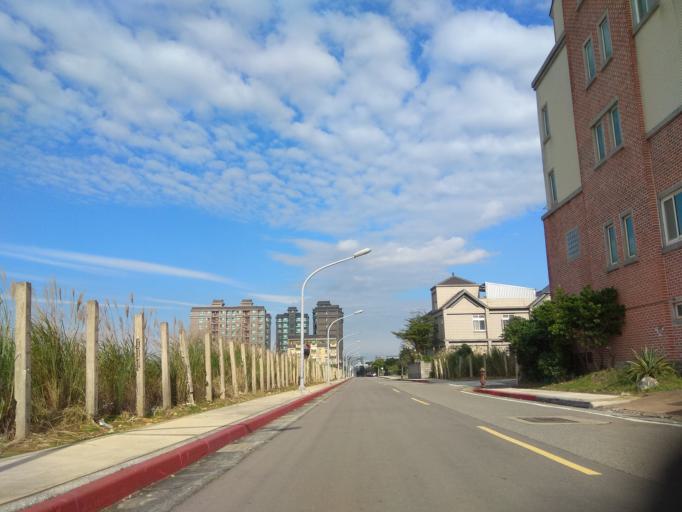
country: TW
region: Taiwan
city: Taoyuan City
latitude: 25.0523
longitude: 121.1767
